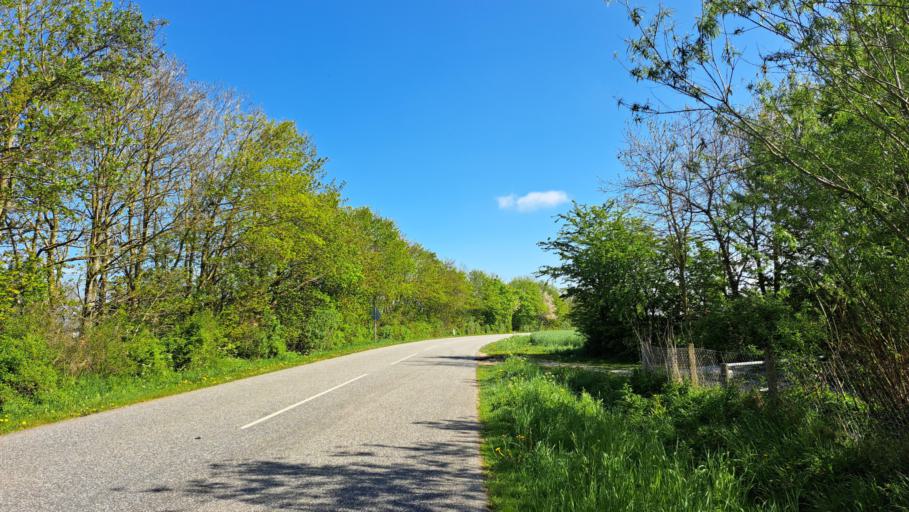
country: DK
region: Central Jutland
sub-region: Hedensted Kommune
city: Hedensted
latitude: 55.7991
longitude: 9.6532
